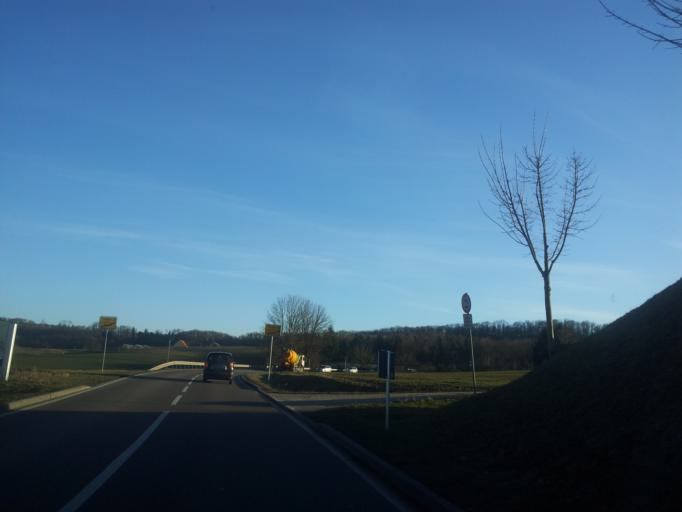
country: DE
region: Baden-Wuerttemberg
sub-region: Regierungsbezirk Stuttgart
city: Flein
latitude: 49.0947
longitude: 9.2181
